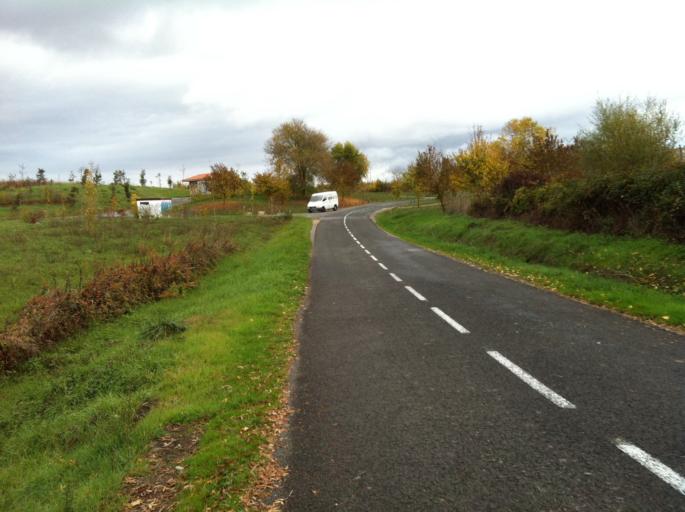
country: ES
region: Basque Country
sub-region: Provincia de Alava
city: Gasteiz / Vitoria
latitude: 42.8725
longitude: -2.6957
